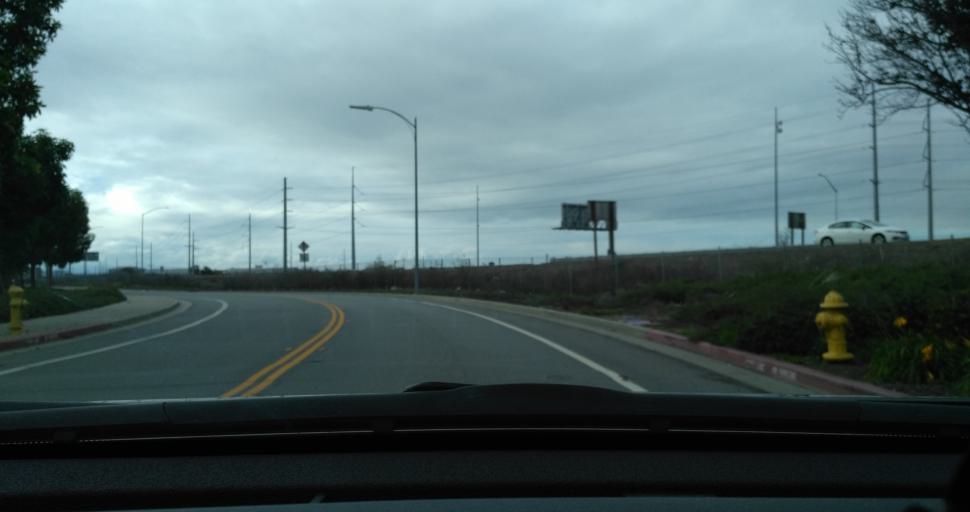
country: US
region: California
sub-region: Santa Clara County
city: Milpitas
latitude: 37.4191
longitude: -121.9414
